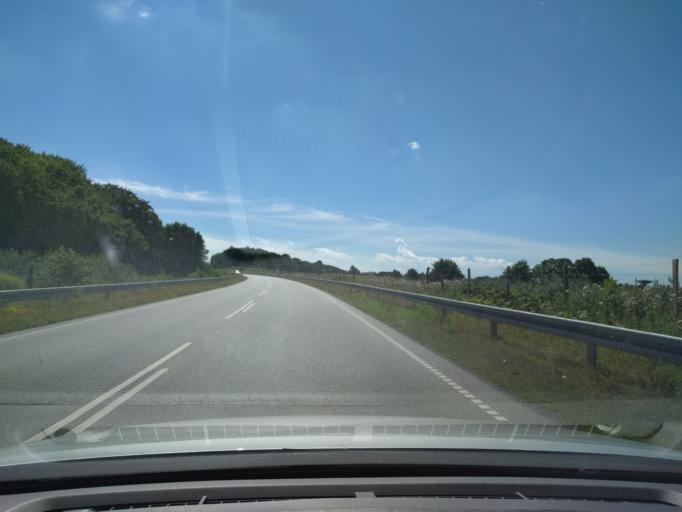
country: DK
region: Zealand
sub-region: Naestved Kommune
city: Fensmark
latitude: 55.2436
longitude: 11.7975
